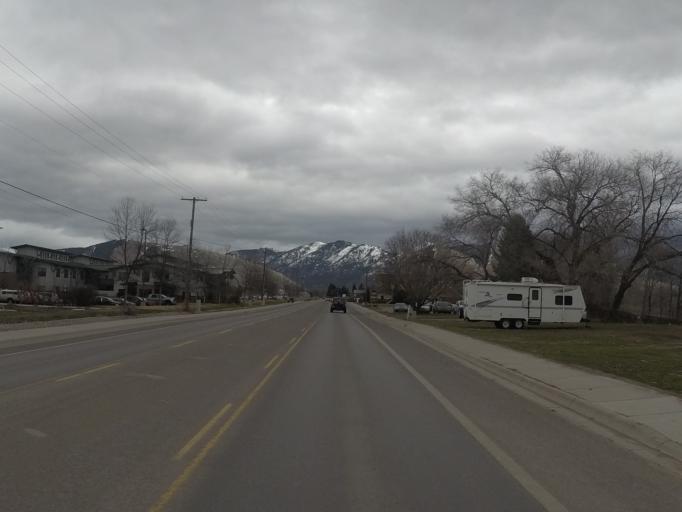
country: US
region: Montana
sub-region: Missoula County
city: Orchard Homes
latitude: 46.8828
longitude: -114.0308
